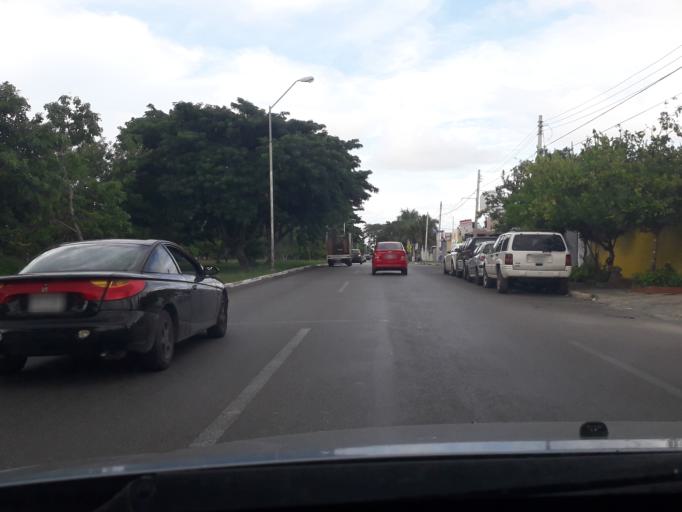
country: MX
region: Yucatan
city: Merida
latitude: 20.9808
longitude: -89.6633
